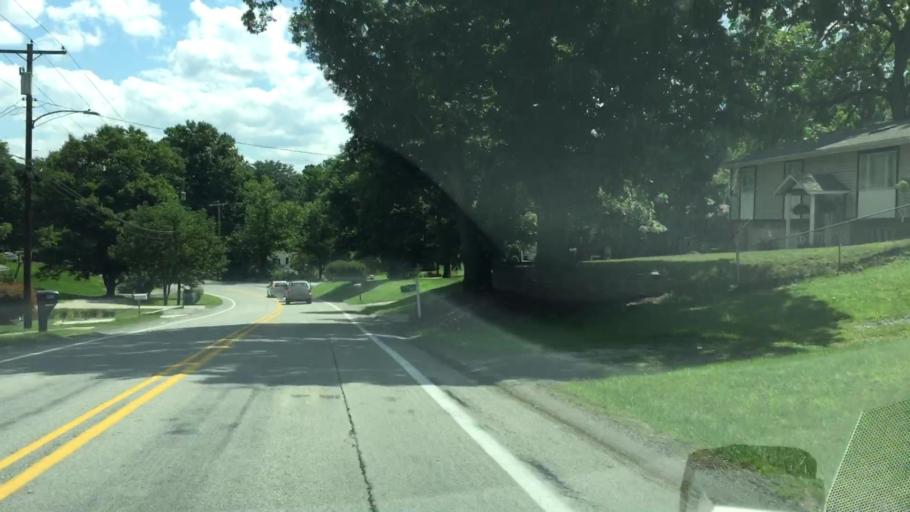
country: US
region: Pennsylvania
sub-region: Allegheny County
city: Bethel Park
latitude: 40.3168
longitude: -80.0453
